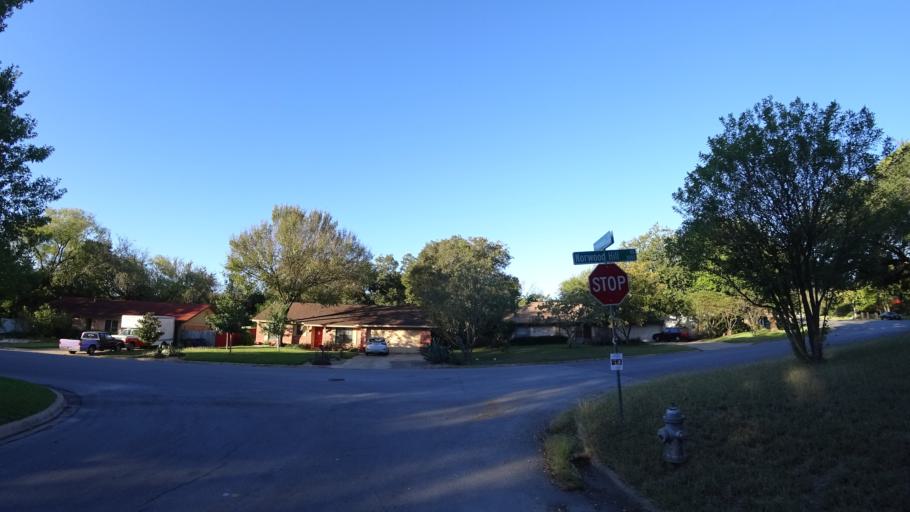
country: US
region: Texas
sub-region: Travis County
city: Austin
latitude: 30.2990
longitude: -97.6799
